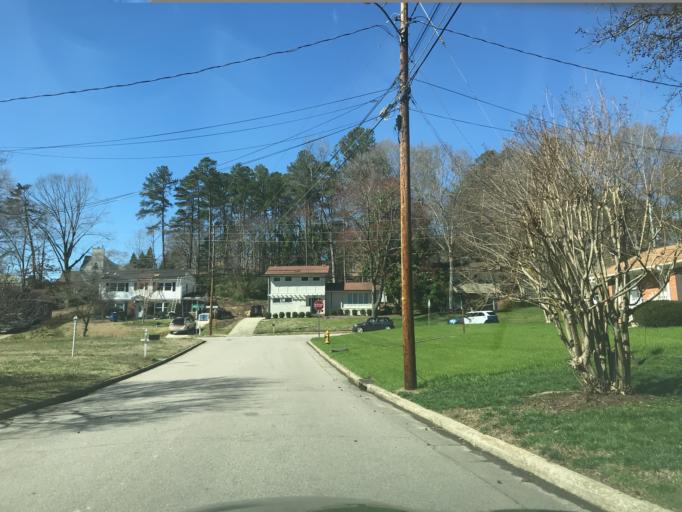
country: US
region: North Carolina
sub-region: Wake County
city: West Raleigh
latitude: 35.8444
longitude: -78.6303
